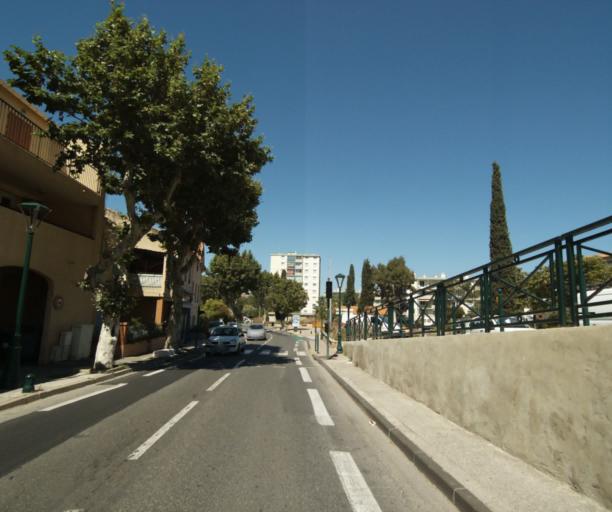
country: FR
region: Provence-Alpes-Cote d'Azur
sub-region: Departement du Var
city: La Garde
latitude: 43.1265
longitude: 6.0126
